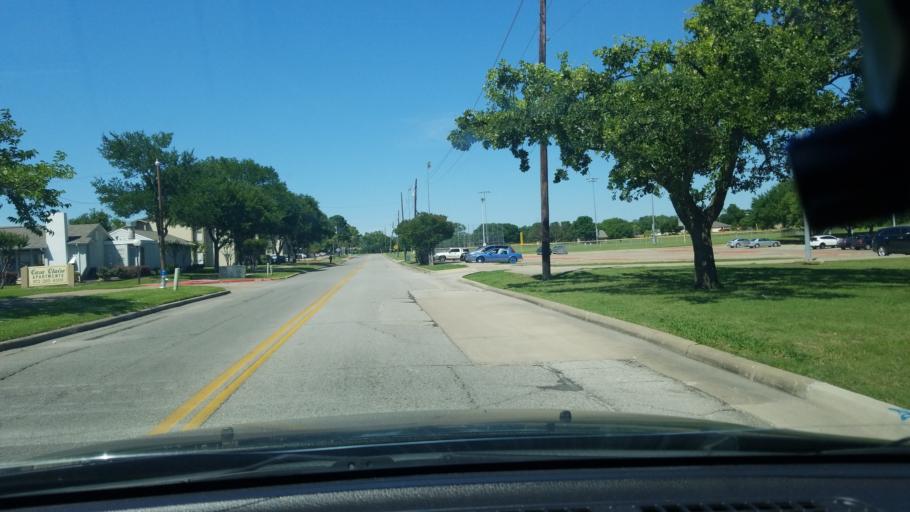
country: US
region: Texas
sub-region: Dallas County
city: Mesquite
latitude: 32.7770
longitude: -96.6172
